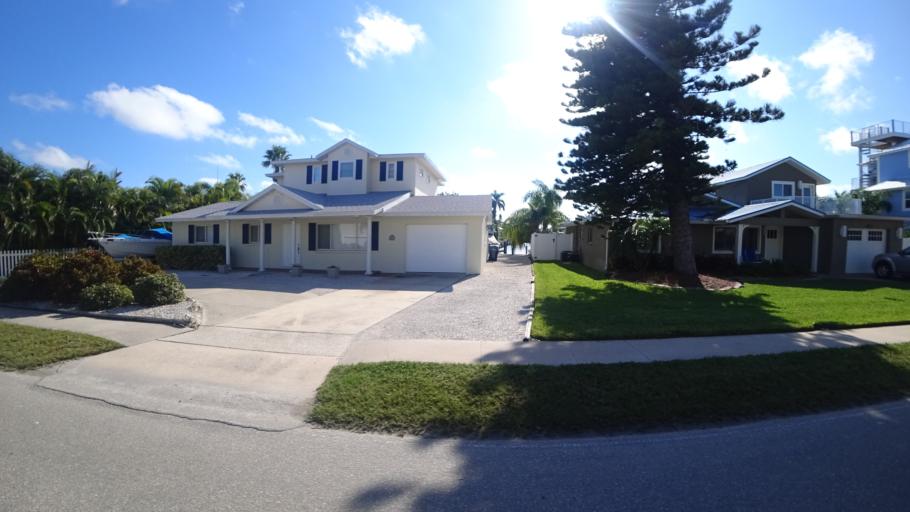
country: US
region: Florida
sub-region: Manatee County
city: Anna Maria
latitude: 27.5310
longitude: -82.7285
